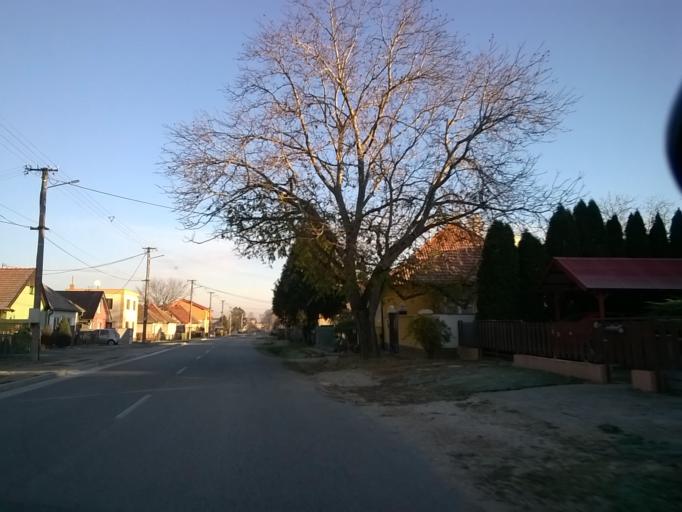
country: SK
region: Nitriansky
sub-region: Okres Nitra
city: Nitra
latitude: 48.4208
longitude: 18.1214
